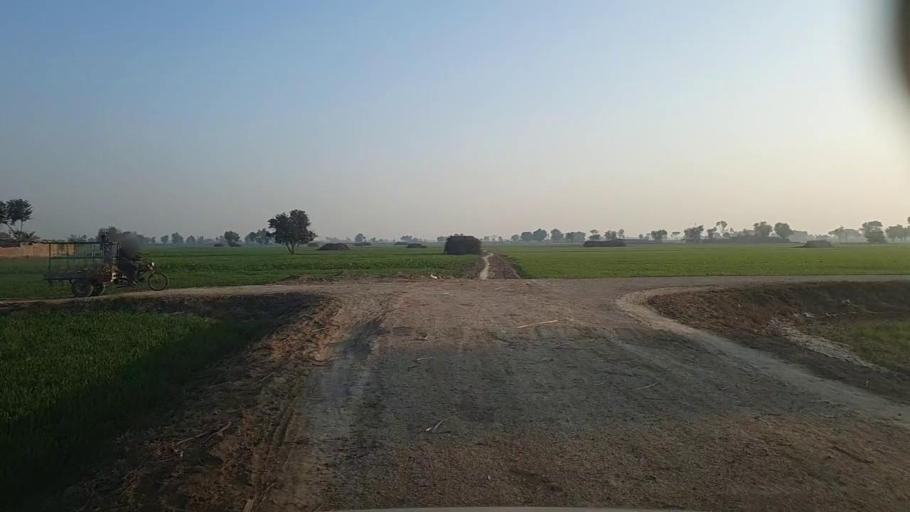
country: PK
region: Sindh
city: Khairpur
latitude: 28.0547
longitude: 69.7590
